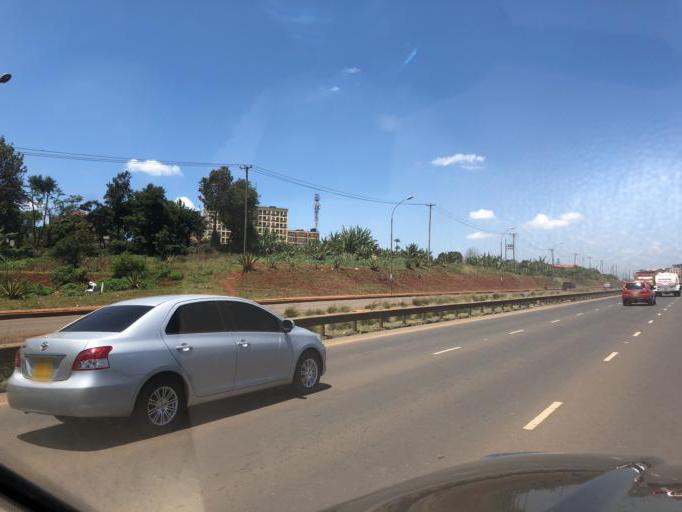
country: KE
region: Kiambu
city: Kiambu
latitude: -1.2129
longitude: 36.9017
